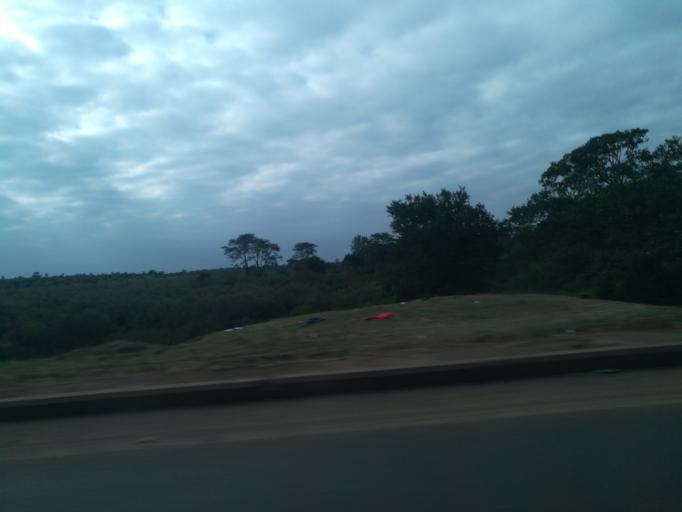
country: KE
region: Nairobi Area
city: Thika
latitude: -1.1290
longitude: 36.9963
